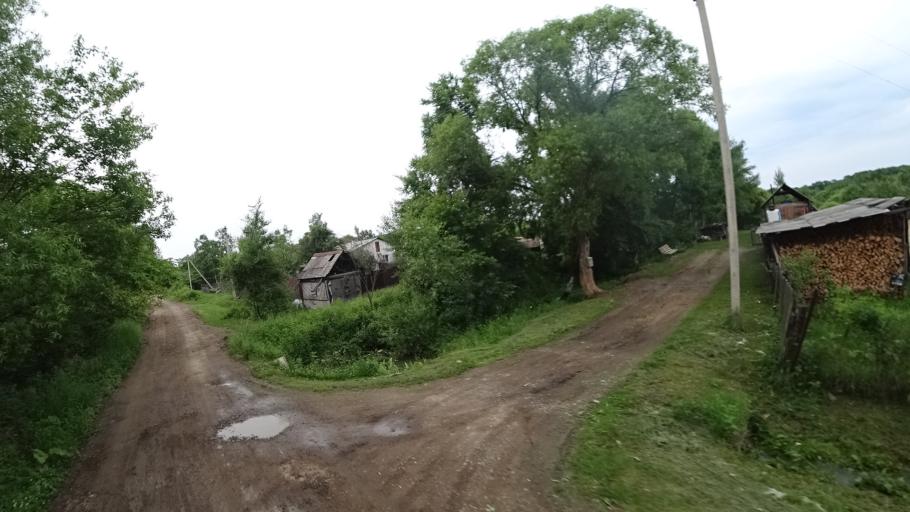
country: RU
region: Primorskiy
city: Novosysoyevka
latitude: 44.2436
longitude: 133.3749
